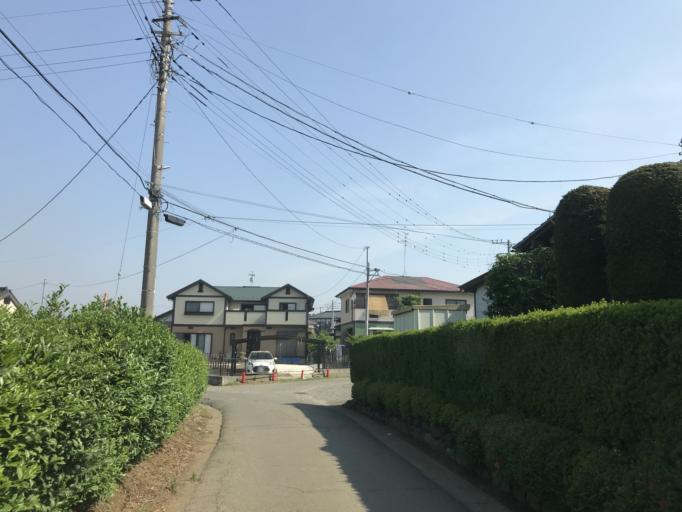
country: JP
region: Ibaraki
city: Mitsukaido
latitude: 36.0482
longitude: 140.0401
